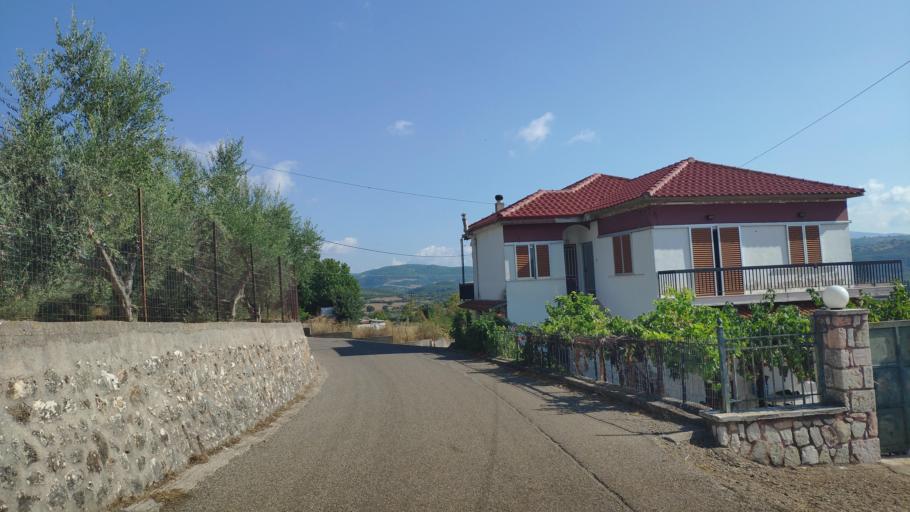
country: GR
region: West Greece
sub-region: Nomos Aitolias kai Akarnanias
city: Fitiai
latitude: 38.6598
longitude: 21.1466
